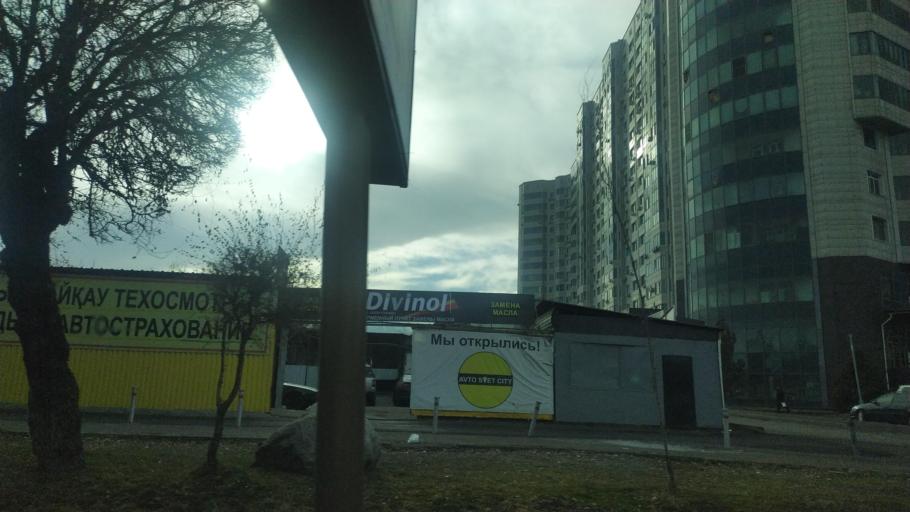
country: KZ
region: Almaty Qalasy
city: Almaty
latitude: 43.2377
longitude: 76.8851
